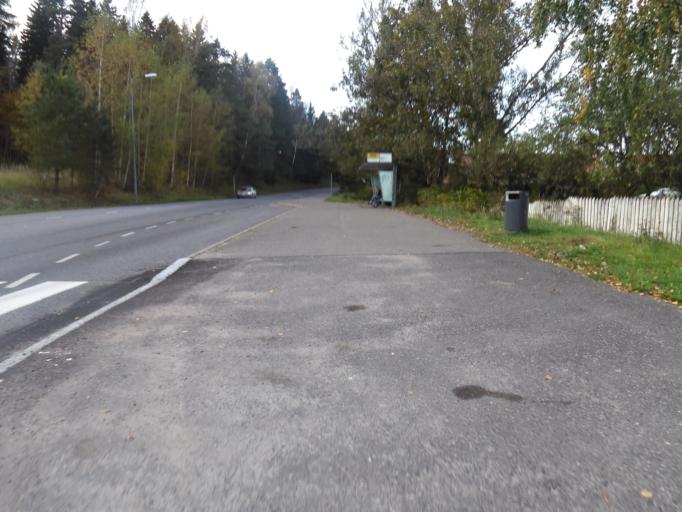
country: FI
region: Uusimaa
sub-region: Helsinki
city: Kilo
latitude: 60.2706
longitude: 24.7535
